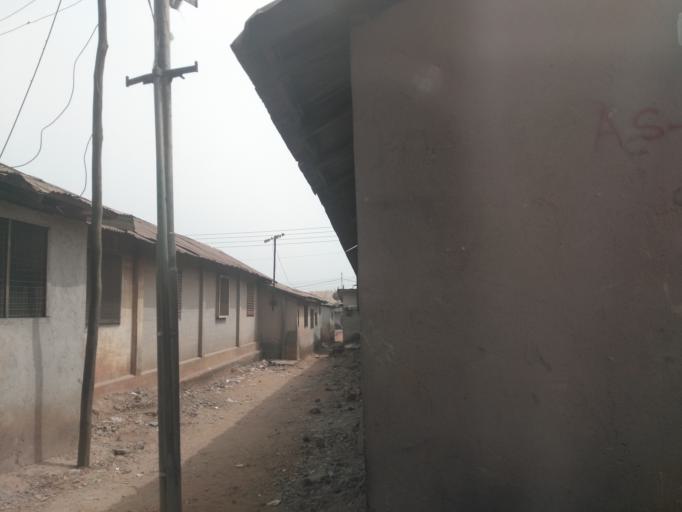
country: GH
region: Ashanti
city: Kumasi
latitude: 6.7025
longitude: -1.6109
